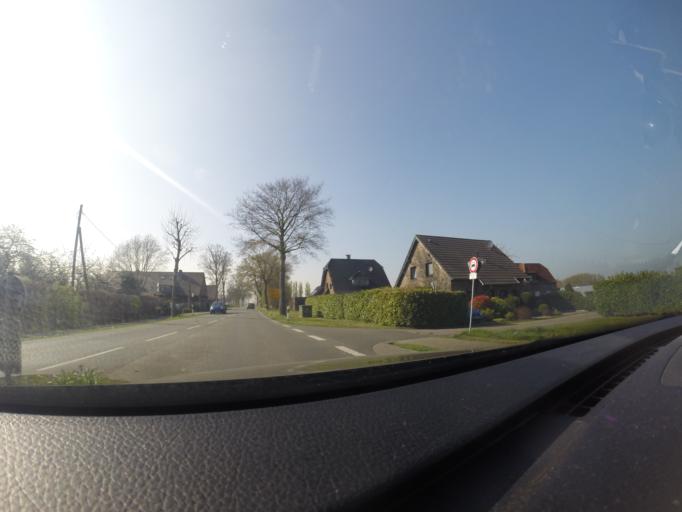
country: DE
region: North Rhine-Westphalia
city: Rees
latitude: 51.7043
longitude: 6.3659
